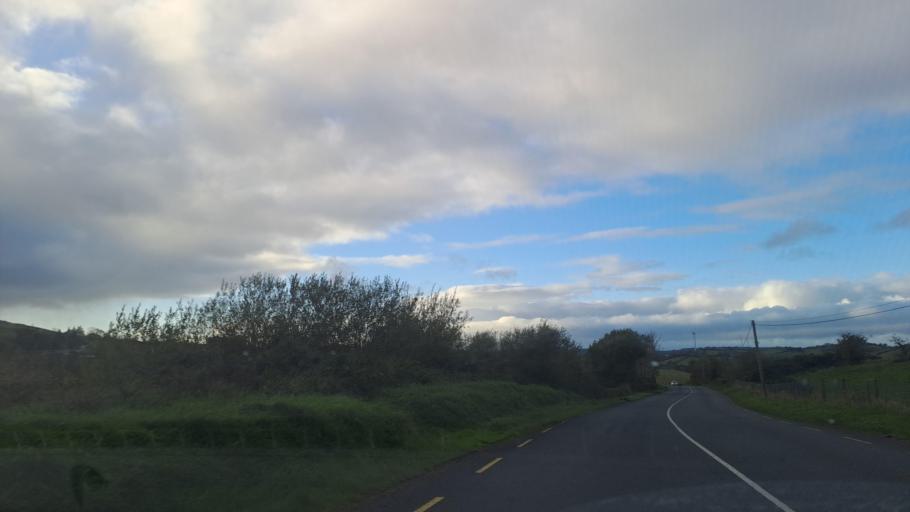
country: IE
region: Ulster
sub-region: County Monaghan
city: Carrickmacross
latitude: 54.0356
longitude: -6.7849
